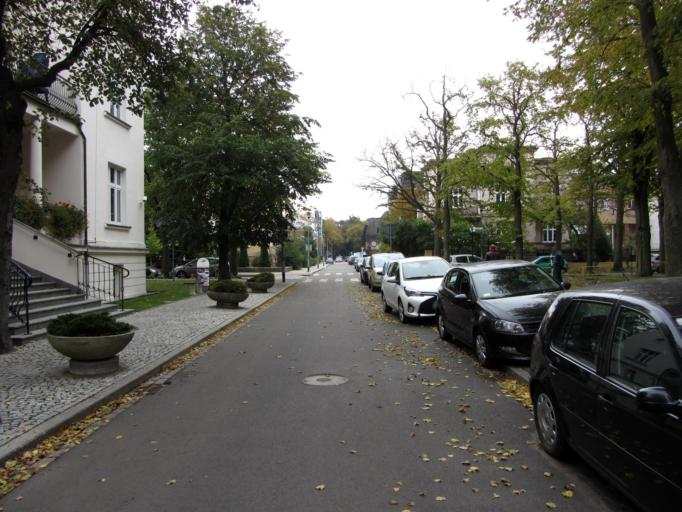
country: PL
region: West Pomeranian Voivodeship
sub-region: Powiat kolobrzeski
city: Kolobrzeg
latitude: 54.1836
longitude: 15.5719
